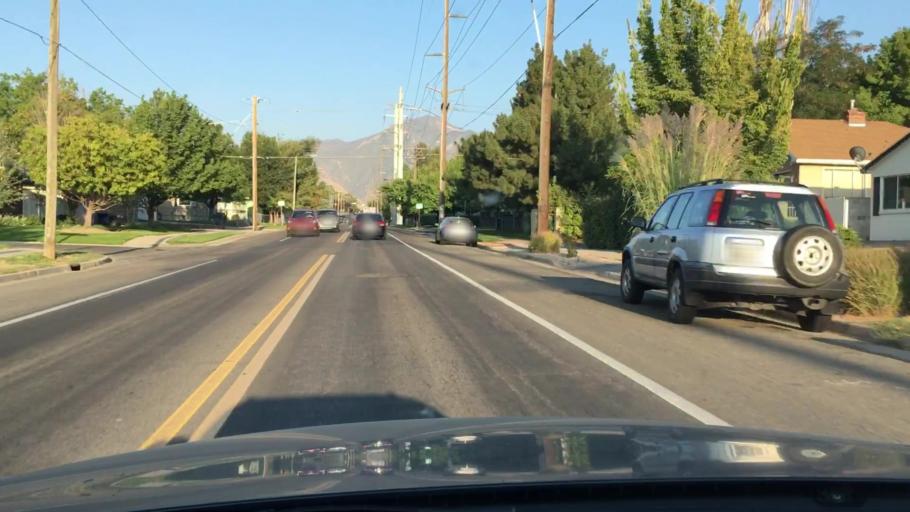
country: US
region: Utah
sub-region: Salt Lake County
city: Willard
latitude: 40.7127
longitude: -111.8607
